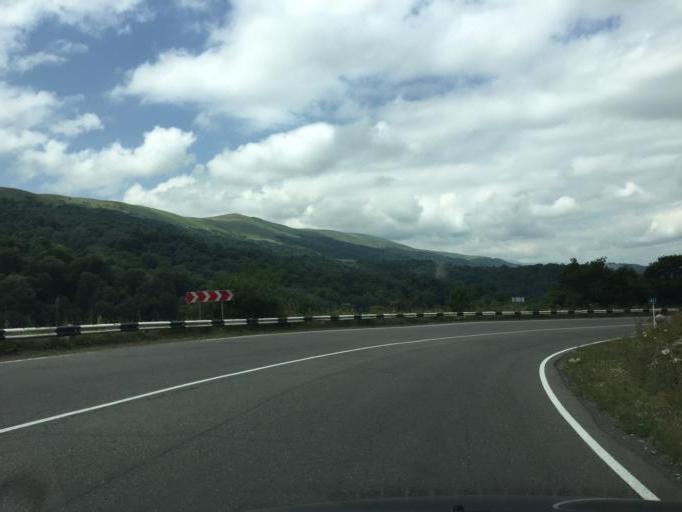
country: AM
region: Tavush
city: Dilijan
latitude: 40.6820
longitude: 44.8715
